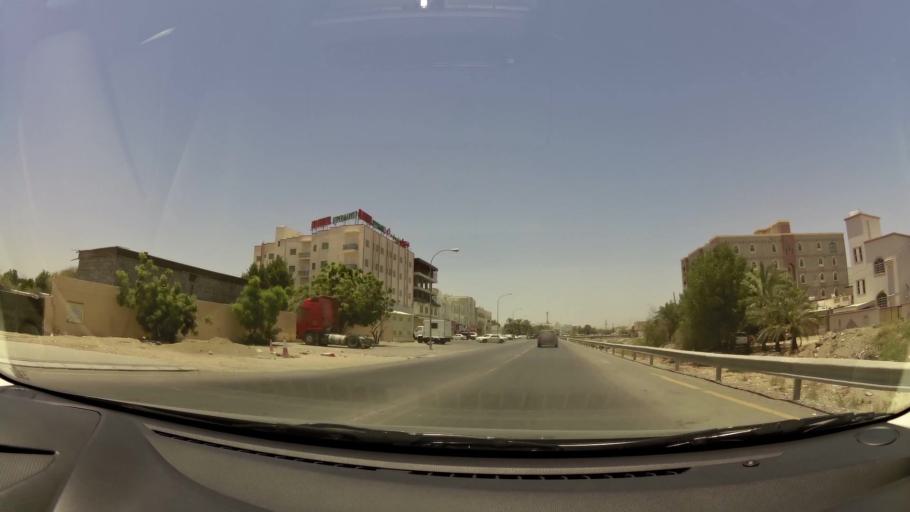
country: OM
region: Muhafazat Masqat
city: As Sib al Jadidah
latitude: 23.6392
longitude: 58.2345
